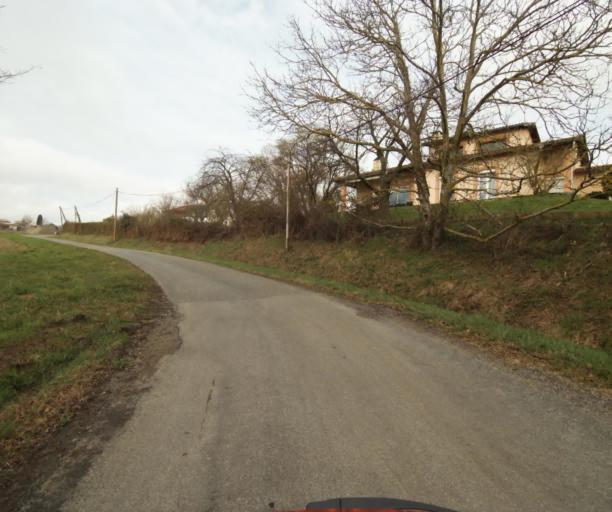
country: FR
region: Midi-Pyrenees
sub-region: Departement de l'Ariege
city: Pamiers
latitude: 43.1037
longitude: 1.5220
